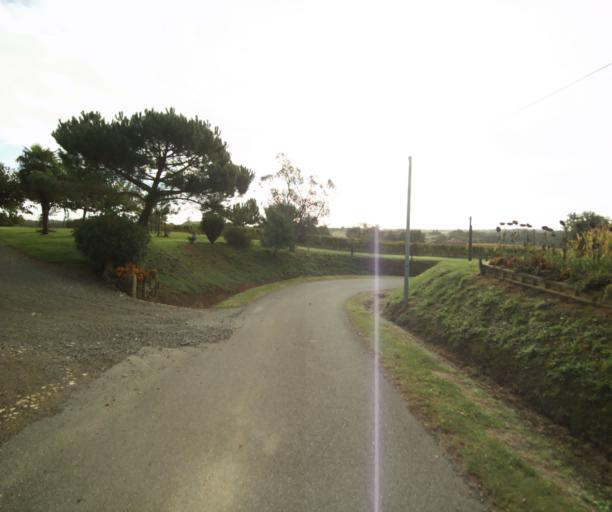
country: FR
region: Midi-Pyrenees
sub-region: Departement du Gers
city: Nogaro
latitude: 43.8120
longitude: -0.0567
